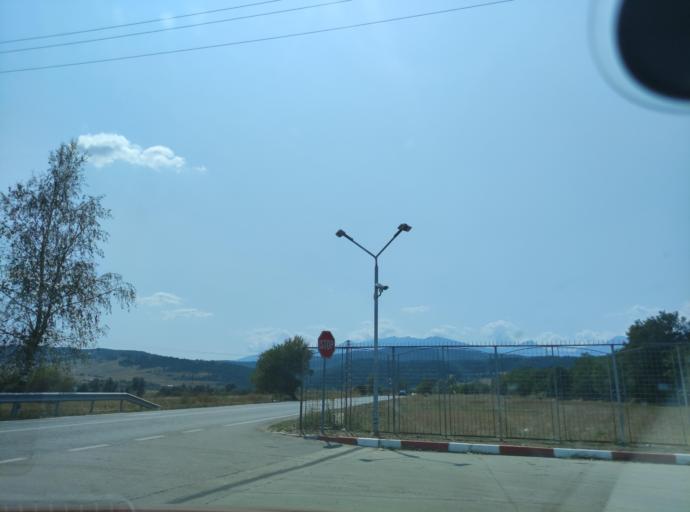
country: BG
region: Blagoevgrad
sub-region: Obshtina Belitsa
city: Belitsa
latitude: 41.9137
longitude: 23.5778
